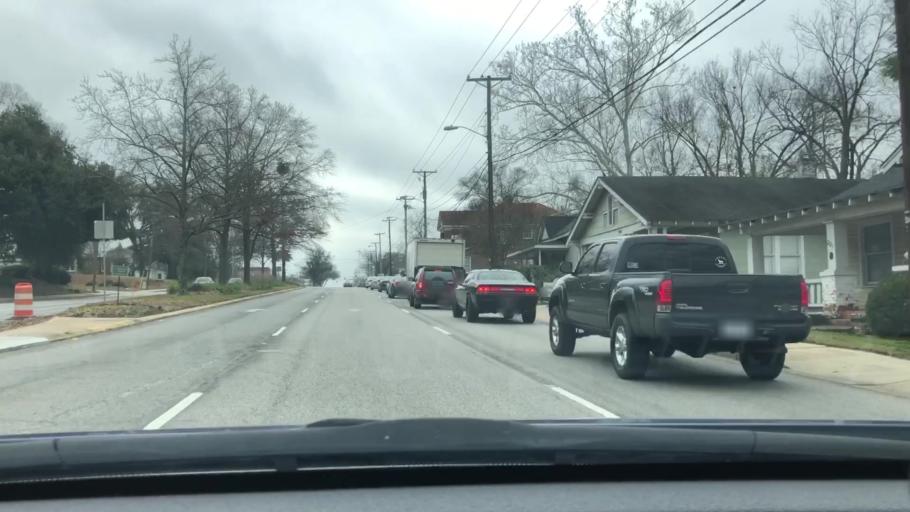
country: US
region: South Carolina
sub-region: Richland County
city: Columbia
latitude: 34.0177
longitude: -81.0355
